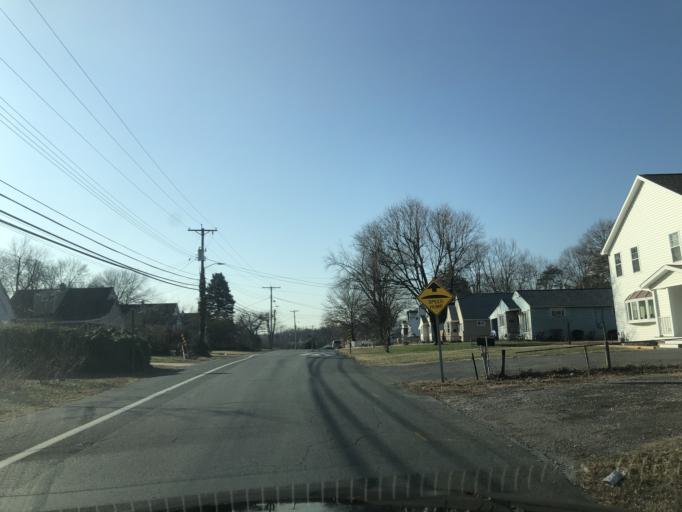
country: US
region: Maryland
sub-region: Anne Arundel County
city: Odenton
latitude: 39.0792
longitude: -76.7009
